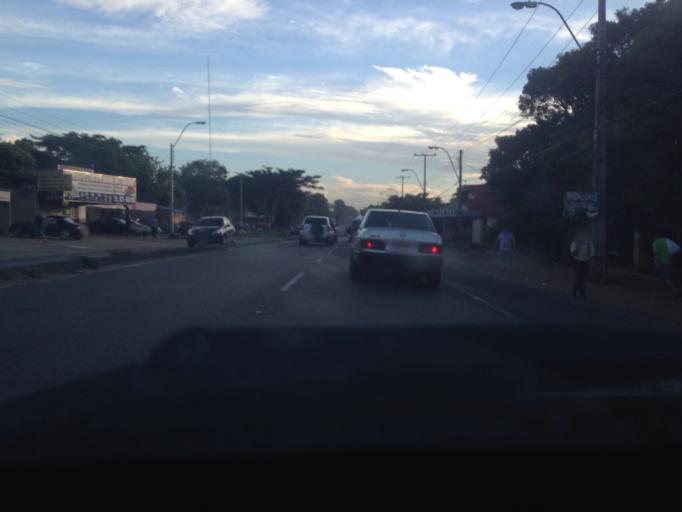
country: PY
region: Central
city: Lambare
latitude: -25.3422
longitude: -57.5865
